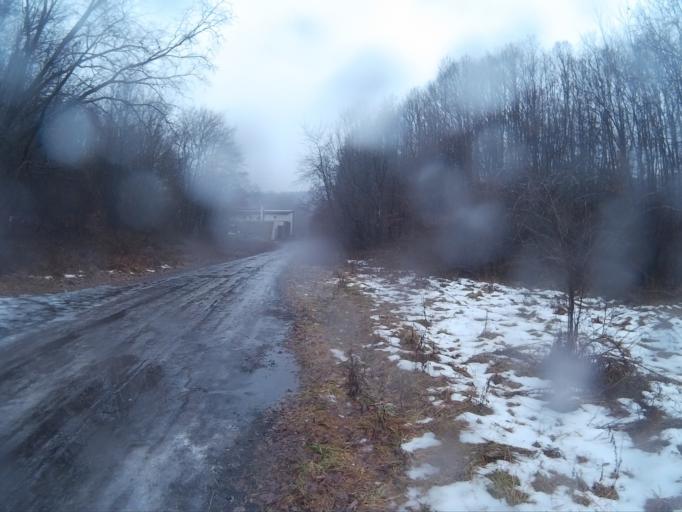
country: HU
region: Nograd
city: Somoskoujfalu
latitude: 48.1573
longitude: 19.8528
